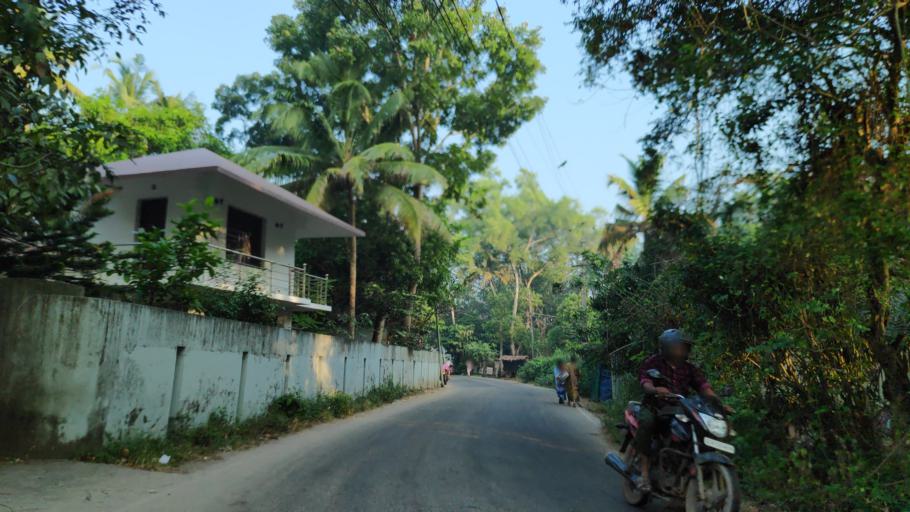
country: IN
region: Kerala
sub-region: Alappuzha
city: Vayalar
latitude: 9.6642
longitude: 76.2988
